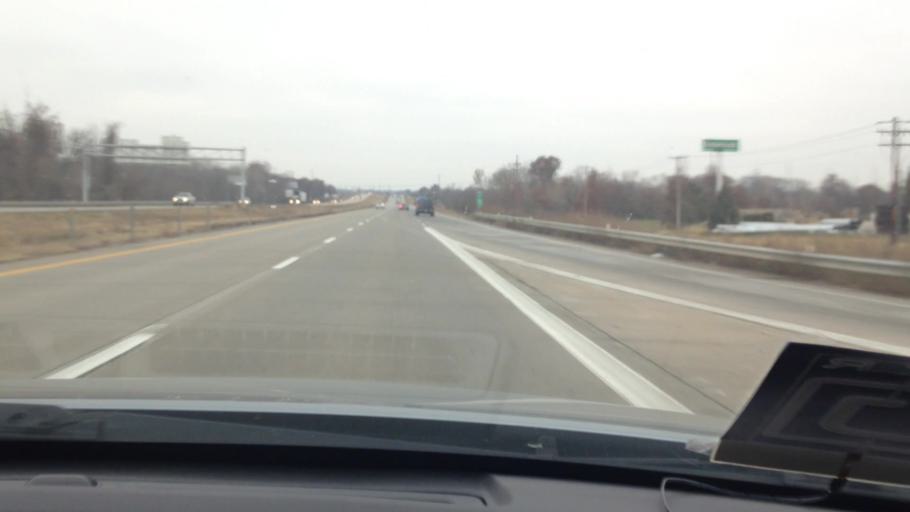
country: US
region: Missouri
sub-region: Cass County
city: Harrisonville
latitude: 38.6382
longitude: -94.3551
